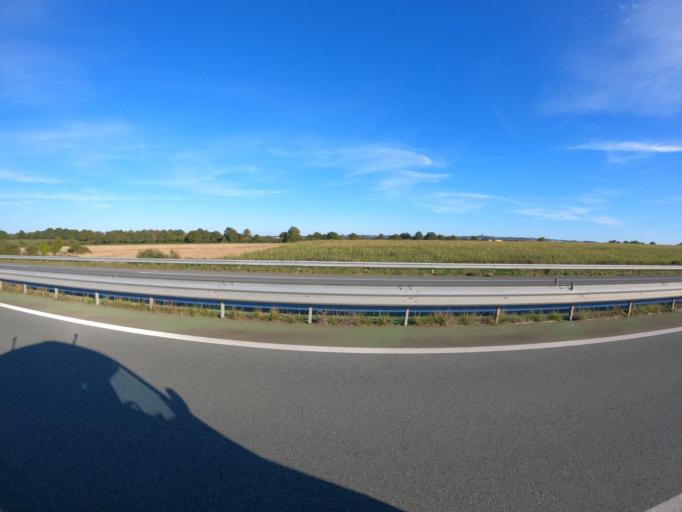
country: FR
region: Pays de la Loire
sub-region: Departement de Maine-et-Loire
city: Chemille-Melay
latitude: 47.1855
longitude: -0.7790
